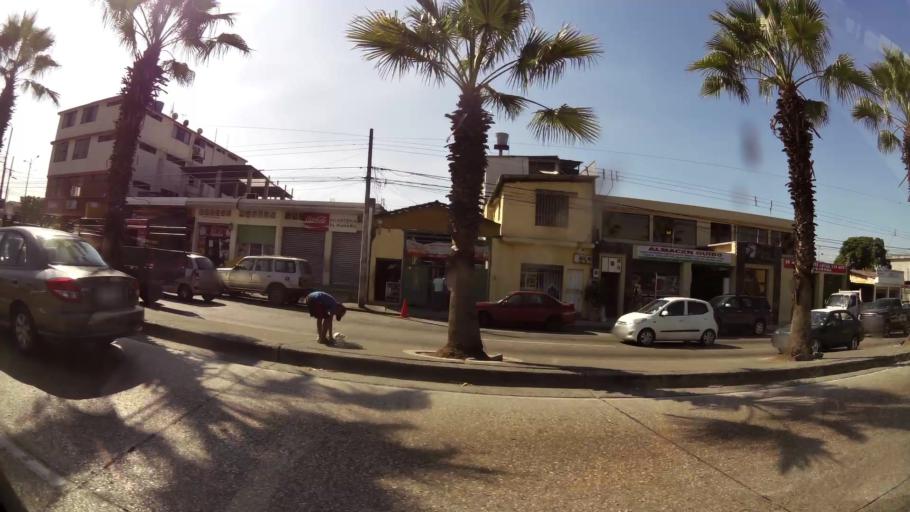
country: EC
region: Guayas
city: Eloy Alfaro
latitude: -2.1331
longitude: -79.9076
